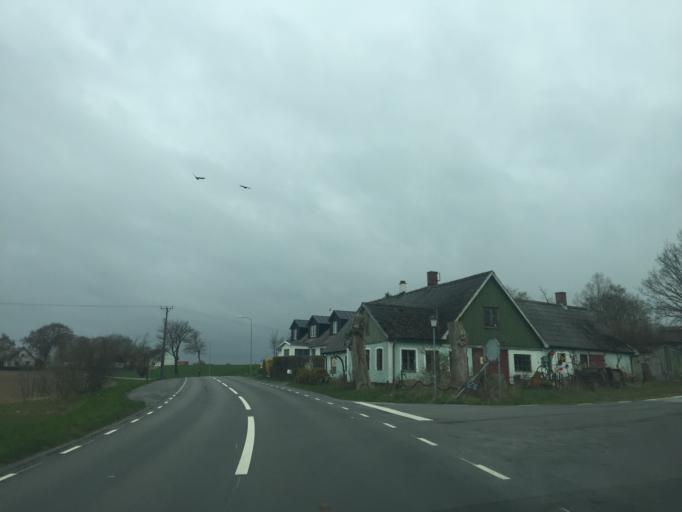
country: SE
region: Skane
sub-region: Skurups Kommun
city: Skivarp
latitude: 55.4228
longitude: 13.6224
